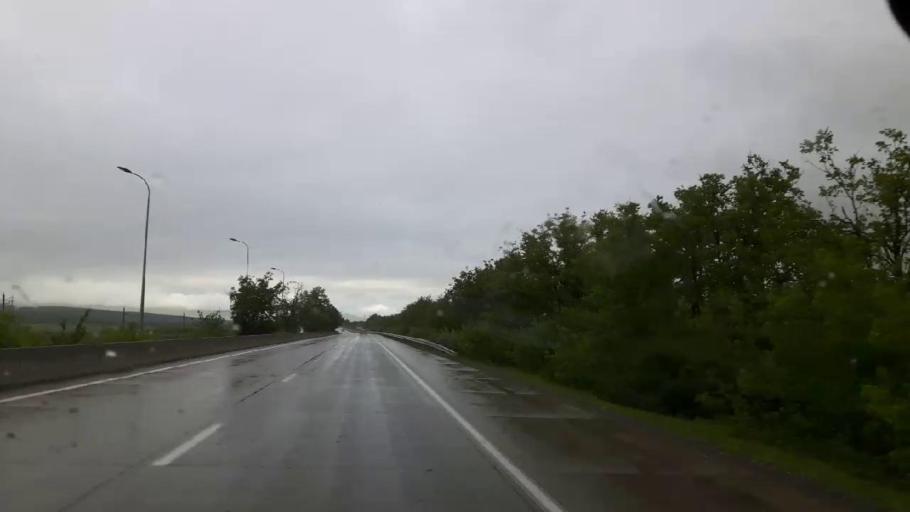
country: GE
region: Shida Kartli
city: Kaspi
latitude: 42.0202
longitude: 44.3055
